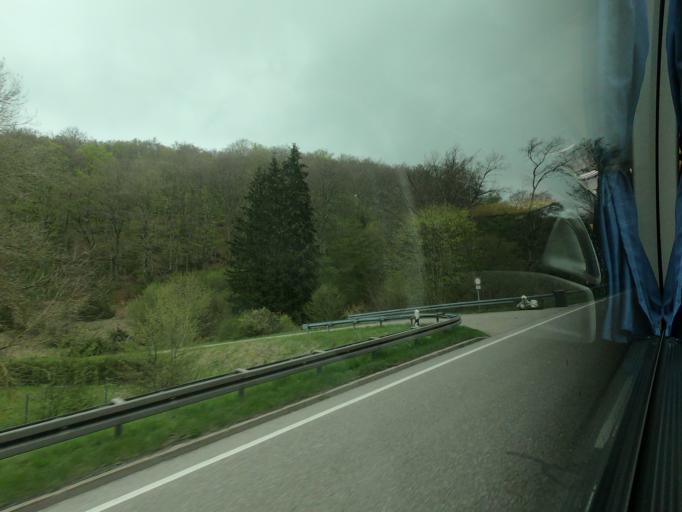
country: DE
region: Baden-Wuerttemberg
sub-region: Regierungsbezirk Stuttgart
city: Nattheim
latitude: 48.6943
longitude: 10.2025
